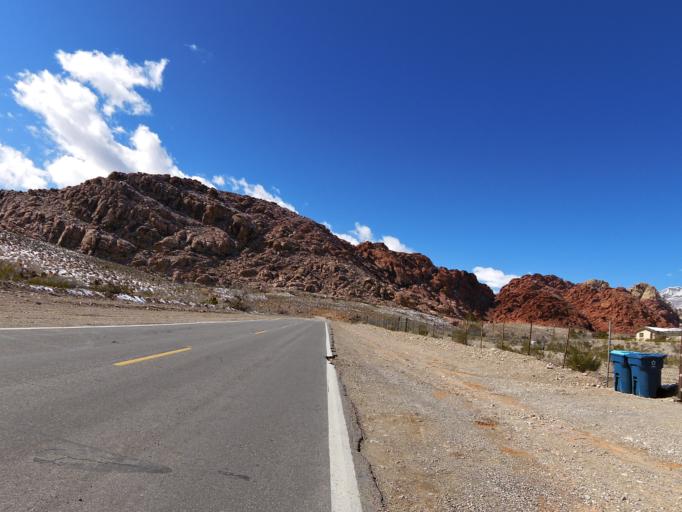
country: US
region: Nevada
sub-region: Clark County
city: Summerlin South
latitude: 36.1474
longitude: -115.4143
